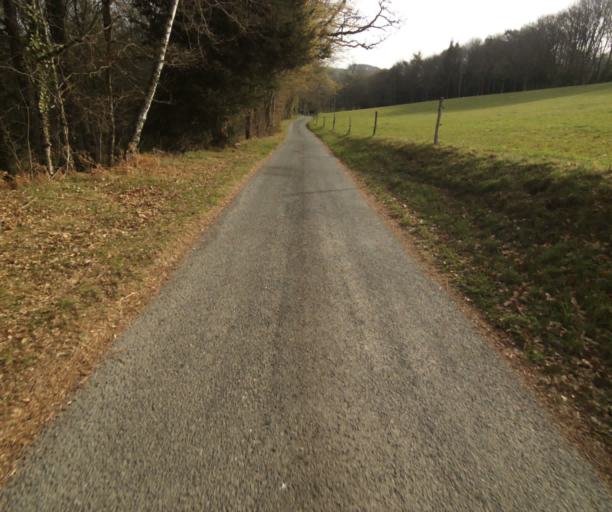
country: FR
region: Limousin
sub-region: Departement de la Correze
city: Chamboulive
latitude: 45.4418
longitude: 1.7507
